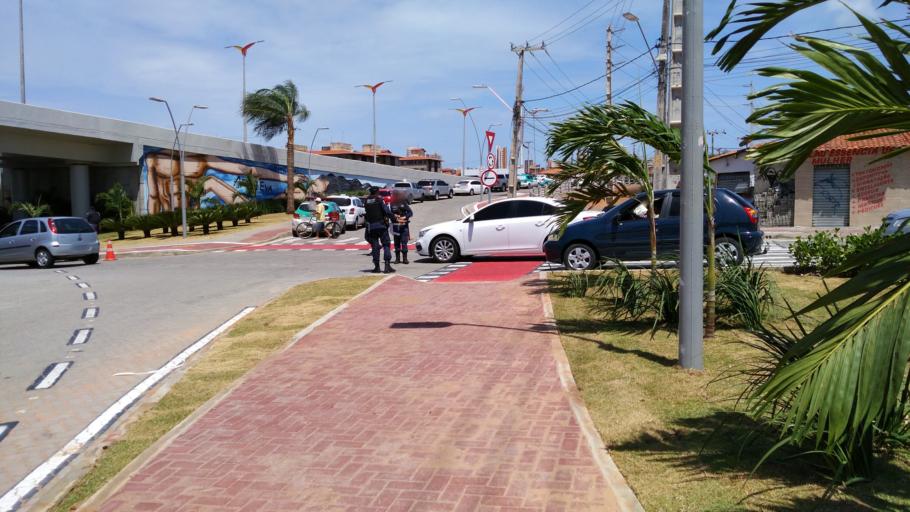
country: BR
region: Ceara
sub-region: Fortaleza
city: Fortaleza
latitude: -3.7640
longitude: -38.5082
